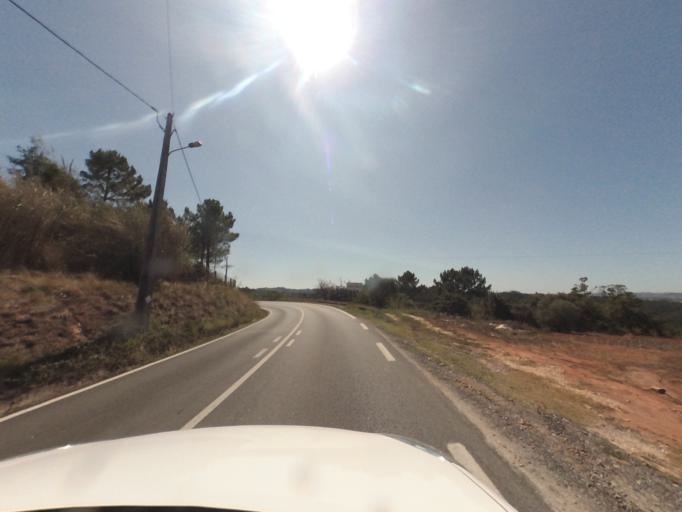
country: PT
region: Leiria
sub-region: Alcobaca
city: Turquel
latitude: 39.5033
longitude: -8.9758
